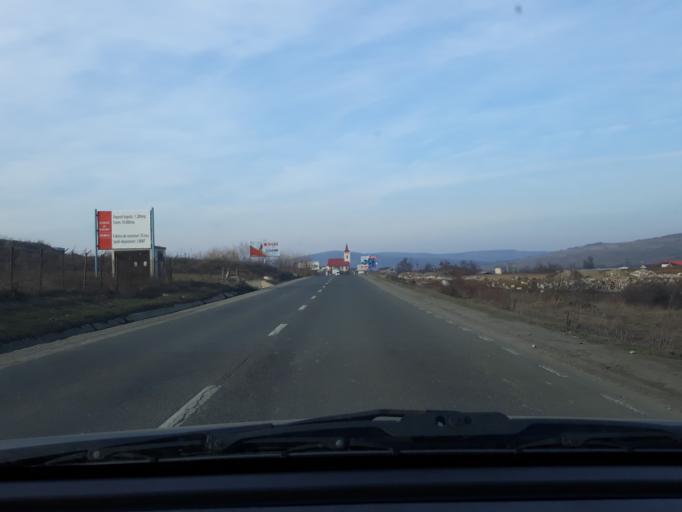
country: RO
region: Salaj
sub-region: Comuna Hereclean
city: Hereclean
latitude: 47.2344
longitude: 22.9955
